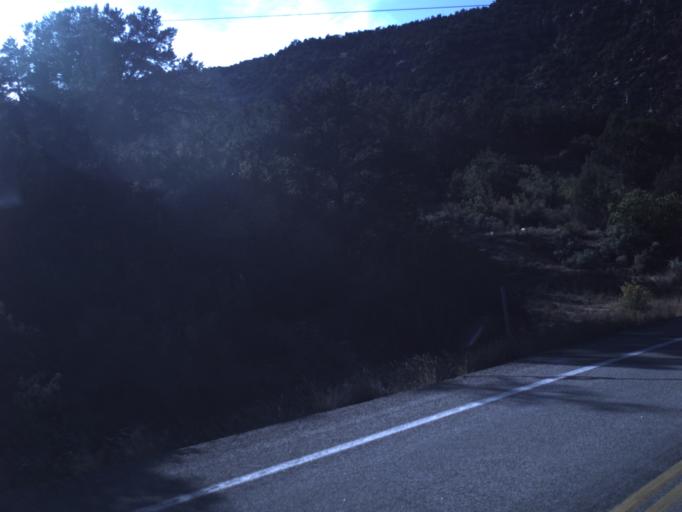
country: US
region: Utah
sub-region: Grand County
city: Moab
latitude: 38.3306
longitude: -109.0895
